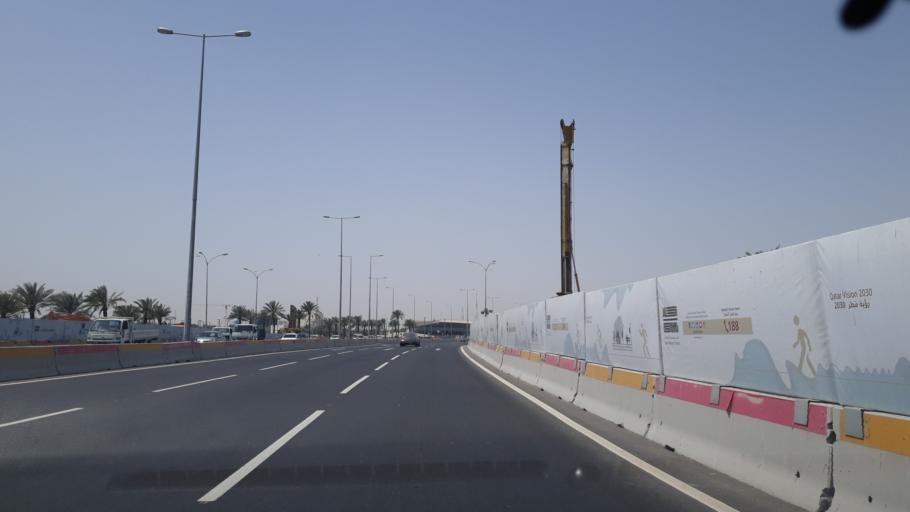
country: QA
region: Baladiyat ad Dawhah
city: Doha
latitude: 25.2954
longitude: 51.5225
